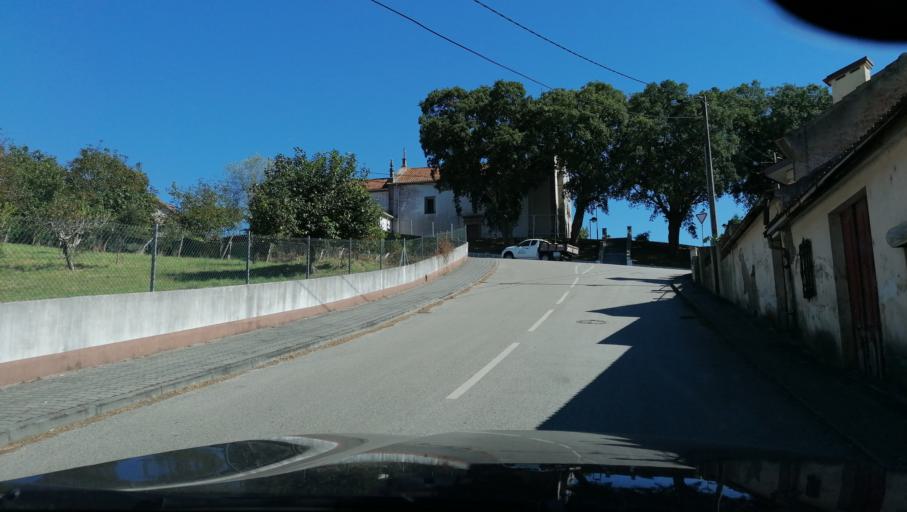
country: PT
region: Aveiro
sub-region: Estarreja
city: Salreu
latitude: 40.7514
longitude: -8.5582
